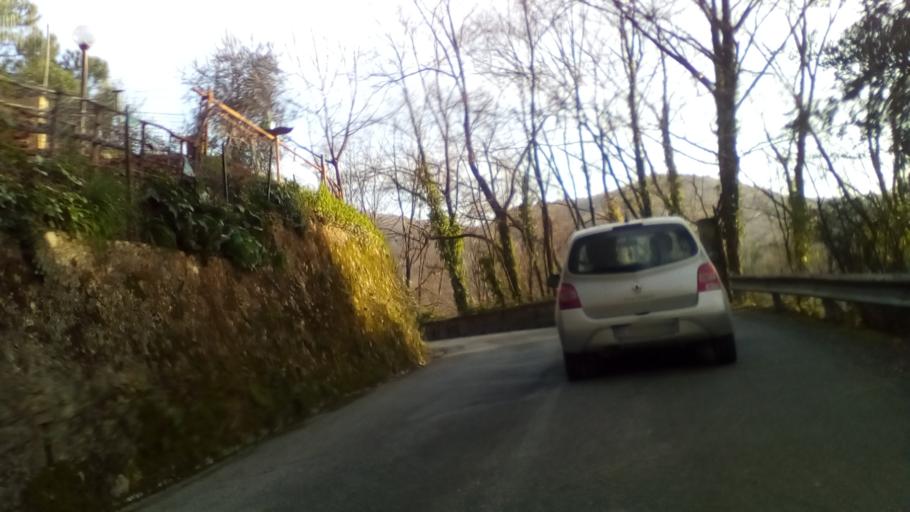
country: IT
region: Tuscany
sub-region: Provincia di Massa-Carrara
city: Massa
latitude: 44.0840
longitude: 10.1178
